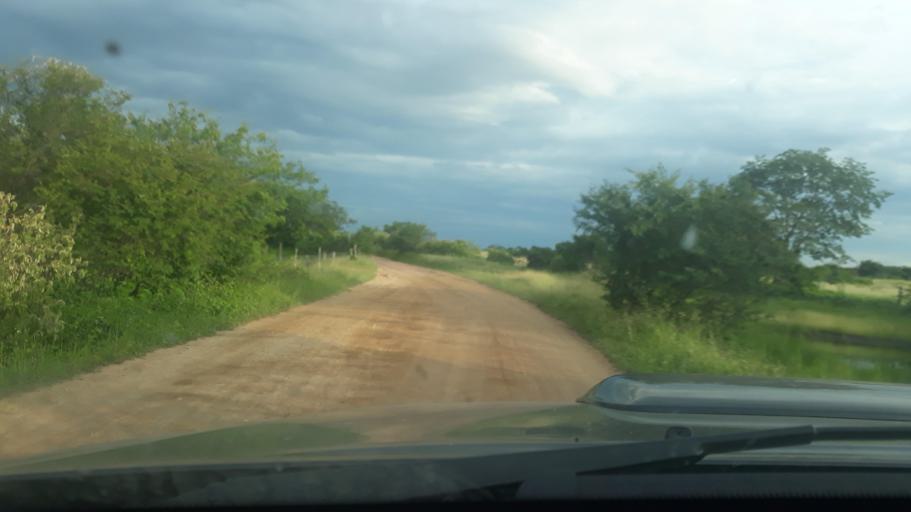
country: BR
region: Bahia
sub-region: Riacho De Santana
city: Riacho de Santana
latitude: -13.9081
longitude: -42.9663
